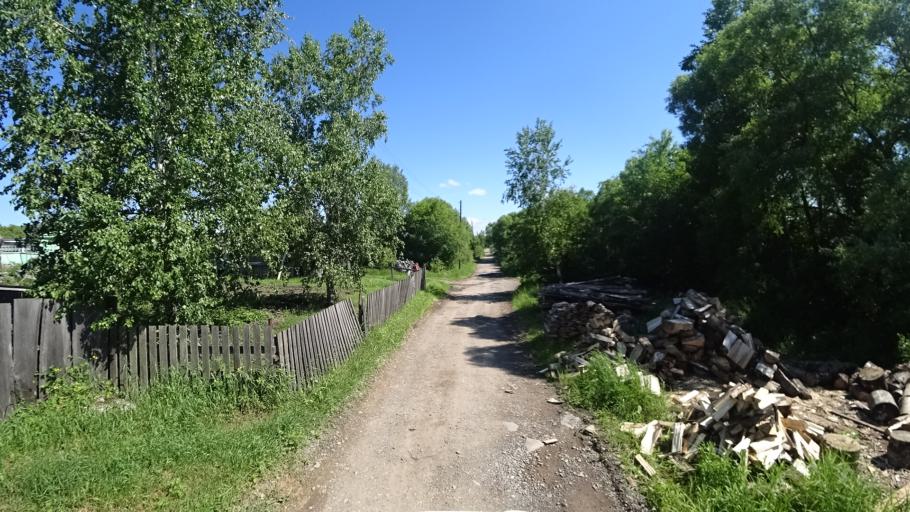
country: RU
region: Khabarovsk Krai
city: Khor
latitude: 47.8871
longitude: 135.0258
